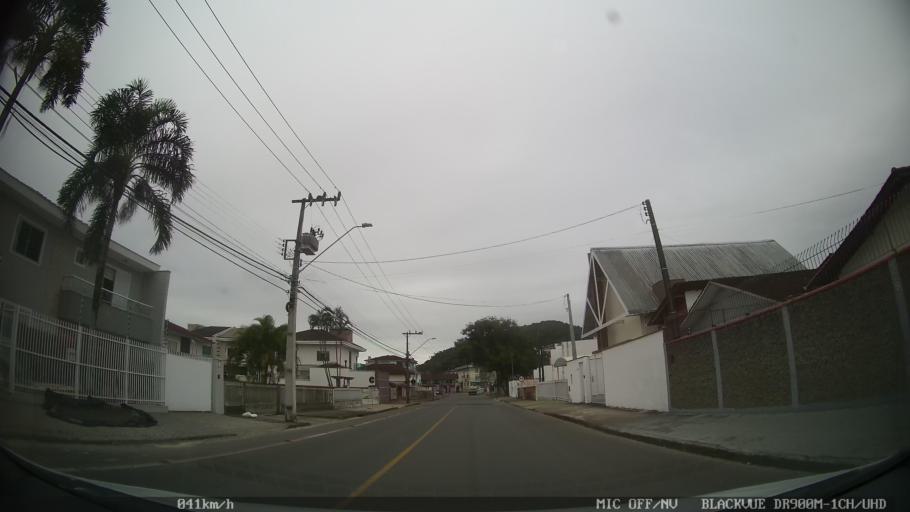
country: BR
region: Santa Catarina
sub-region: Joinville
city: Joinville
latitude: -26.2746
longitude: -48.8346
